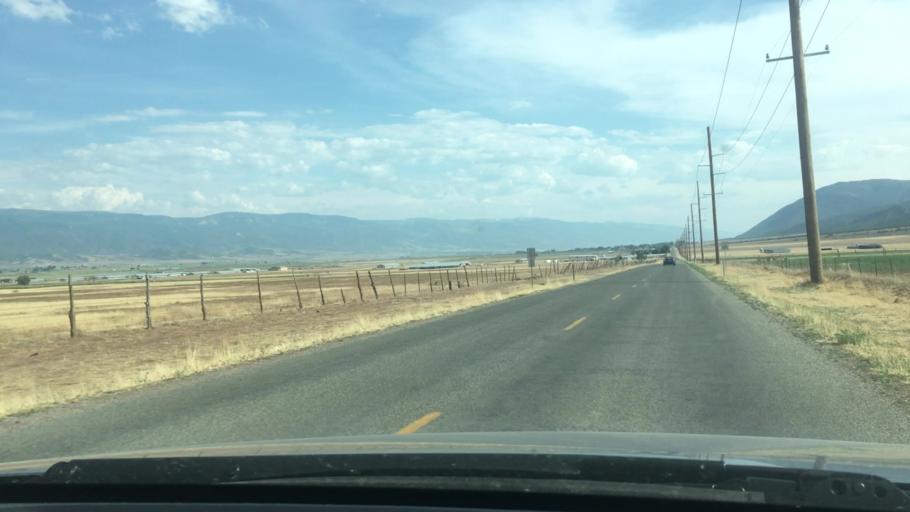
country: US
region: Utah
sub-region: Sanpete County
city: Moroni
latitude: 39.5394
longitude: -111.6400
